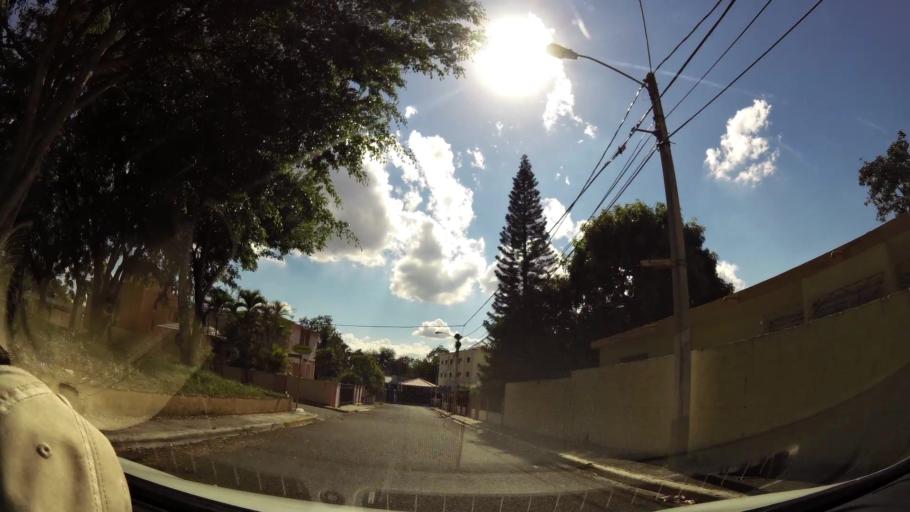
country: DO
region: Santiago
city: Santiago de los Caballeros
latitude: 19.4537
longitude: -70.6672
